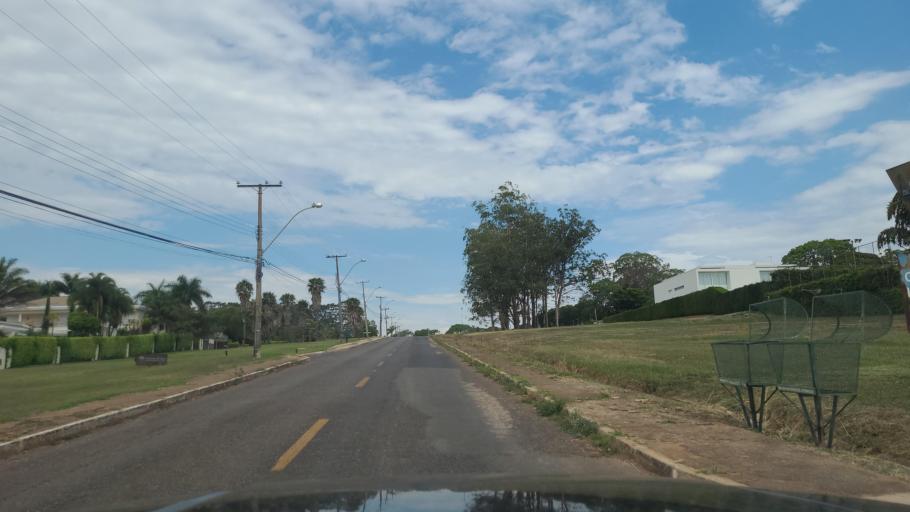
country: BR
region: Federal District
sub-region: Brasilia
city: Brasilia
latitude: -15.8579
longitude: -47.8444
